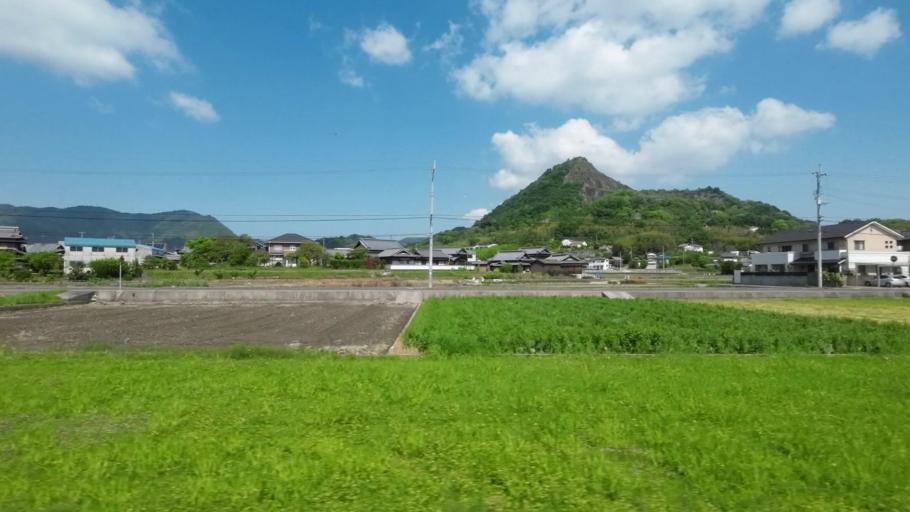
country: JP
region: Kagawa
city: Kan'onjicho
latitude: 34.1807
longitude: 133.7086
